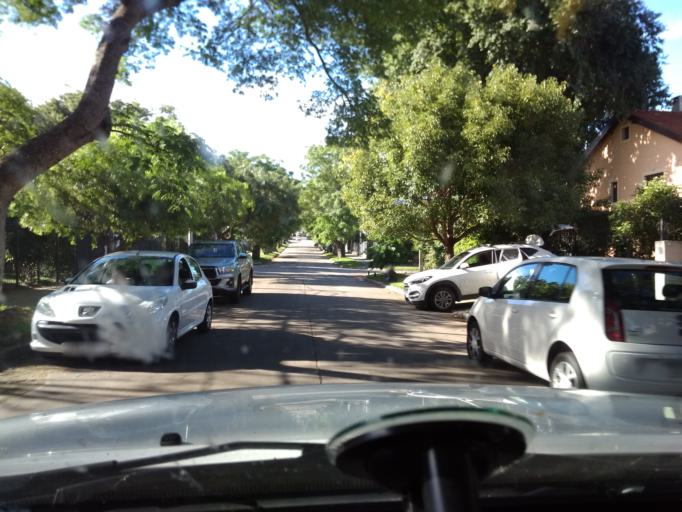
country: UY
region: Canelones
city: Paso de Carrasco
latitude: -34.8874
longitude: -56.0751
